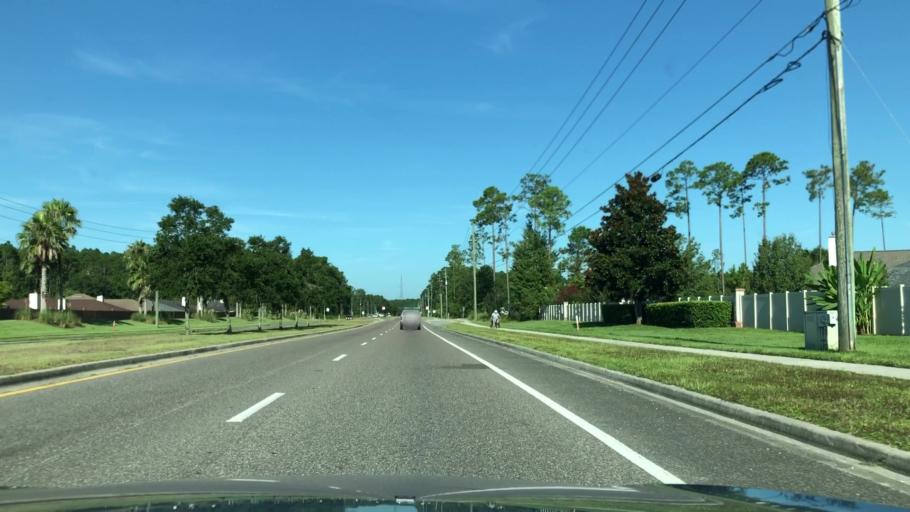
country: US
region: Florida
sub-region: Saint Johns County
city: Fruit Cove
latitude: 30.0601
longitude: -81.5180
